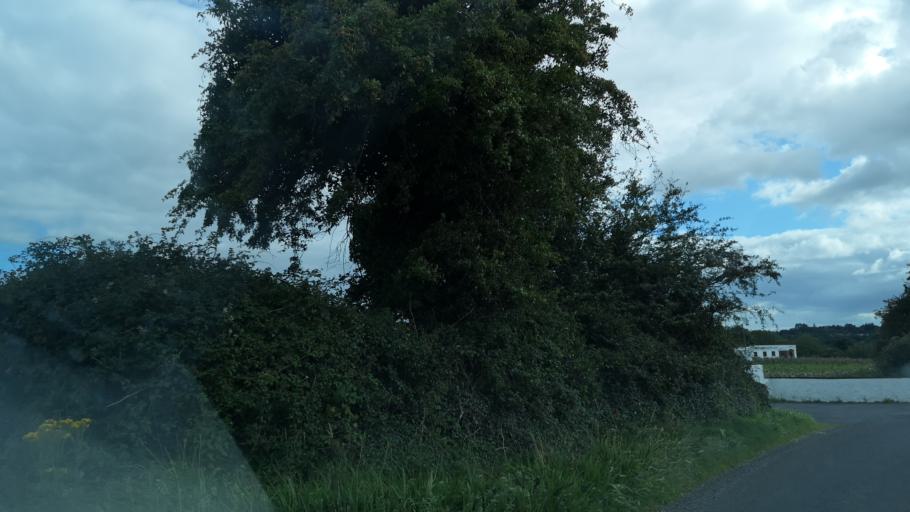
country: IE
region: Connaught
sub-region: County Galway
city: Moycullen
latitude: 53.3462
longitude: -9.1721
